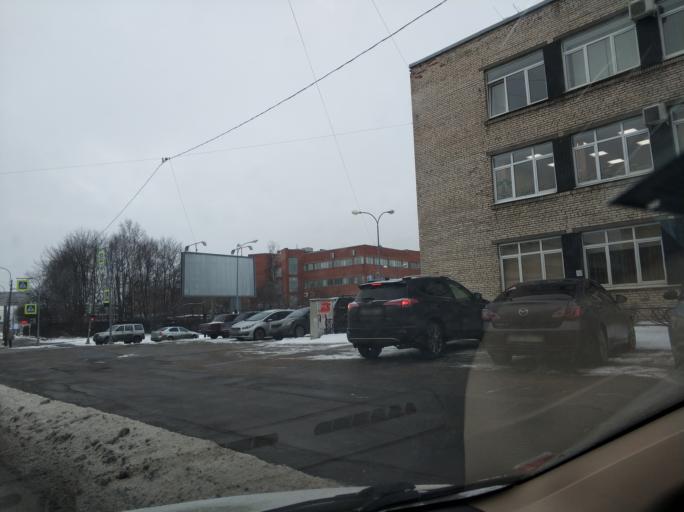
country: RU
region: St.-Petersburg
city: Centralniy
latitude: 59.9172
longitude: 30.3744
